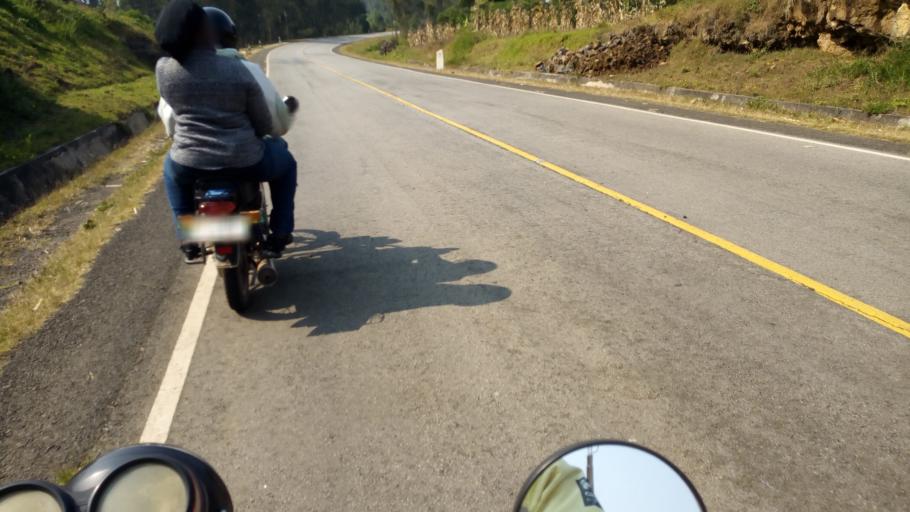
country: UG
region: Western Region
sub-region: Kisoro District
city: Kisoro
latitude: -1.3195
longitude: 29.7274
